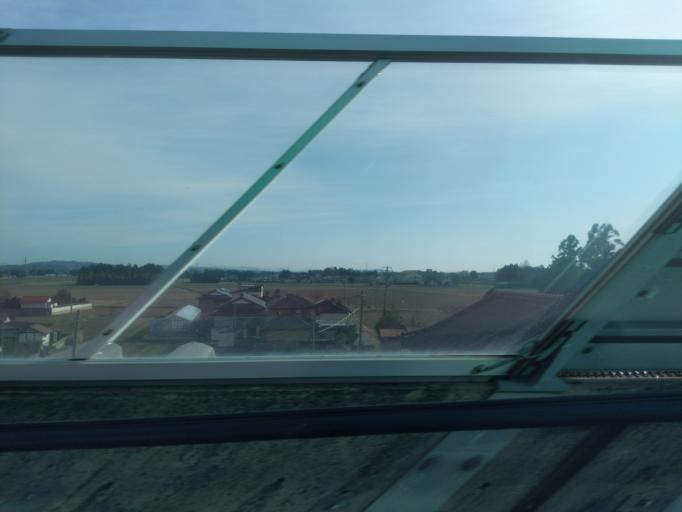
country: JP
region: Miyagi
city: Furukawa
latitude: 38.5978
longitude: 140.9809
